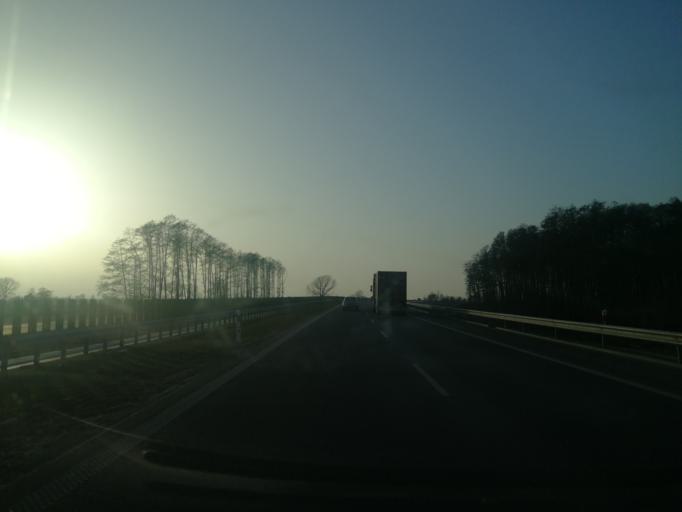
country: PL
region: Warmian-Masurian Voivodeship
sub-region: Powiat elblaski
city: Gronowo Elblaskie
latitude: 54.1646
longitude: 19.2518
